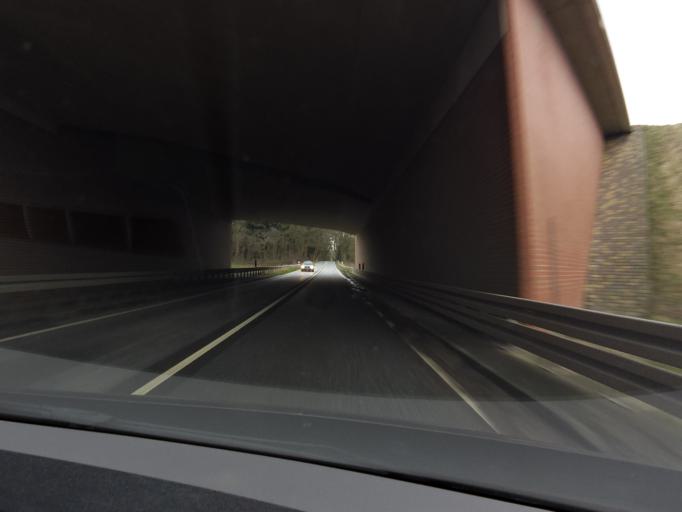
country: DE
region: Mecklenburg-Vorpommern
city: Carlow
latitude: 53.8167
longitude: 10.8999
